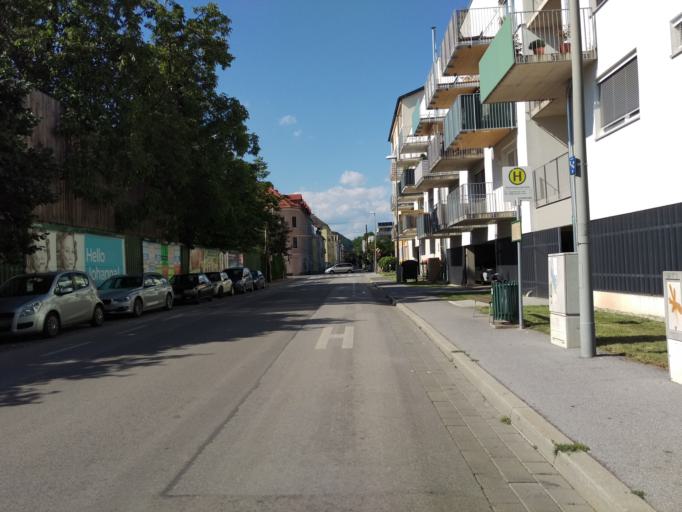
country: AT
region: Styria
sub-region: Graz Stadt
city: Wetzelsdorf
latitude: 47.0630
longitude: 15.4033
